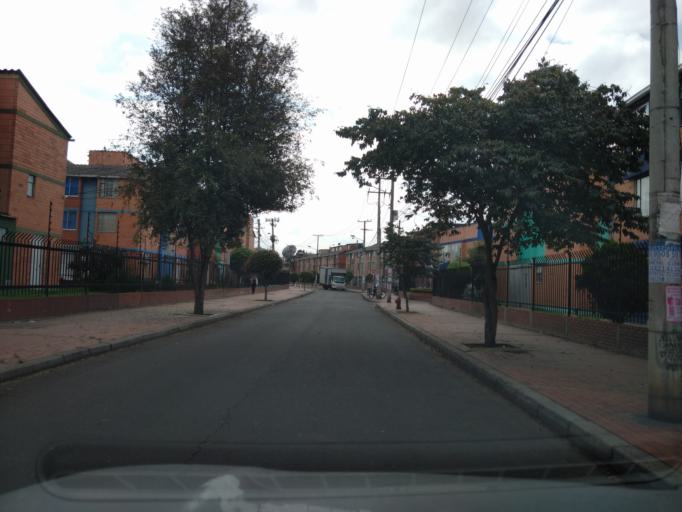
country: CO
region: Cundinamarca
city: Funza
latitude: 4.6699
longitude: -74.1589
